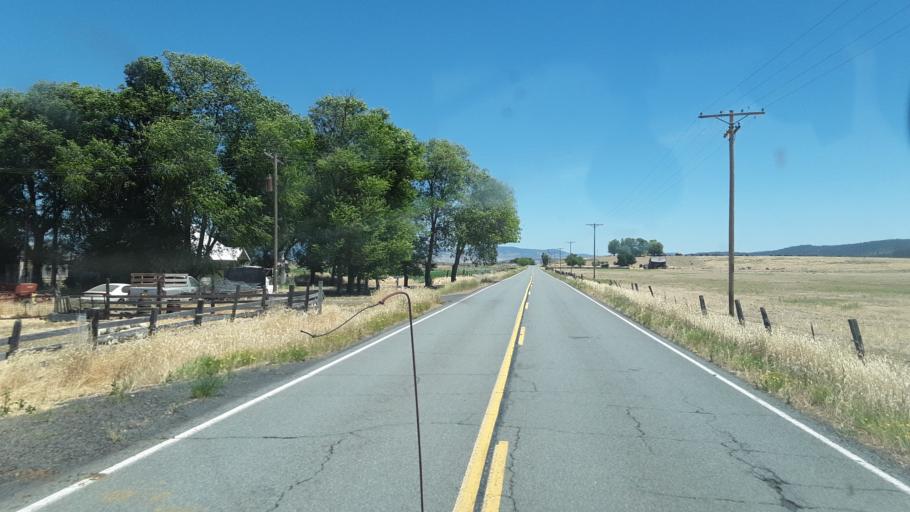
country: US
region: California
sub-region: Shasta County
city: Burney
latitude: 41.1320
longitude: -121.0964
